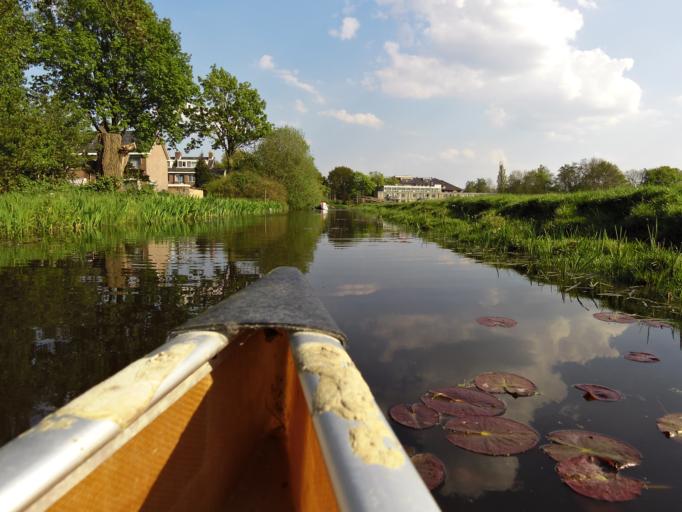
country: NL
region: South Holland
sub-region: Gemeente Voorschoten
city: Voorschoten
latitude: 52.1331
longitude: 4.4455
